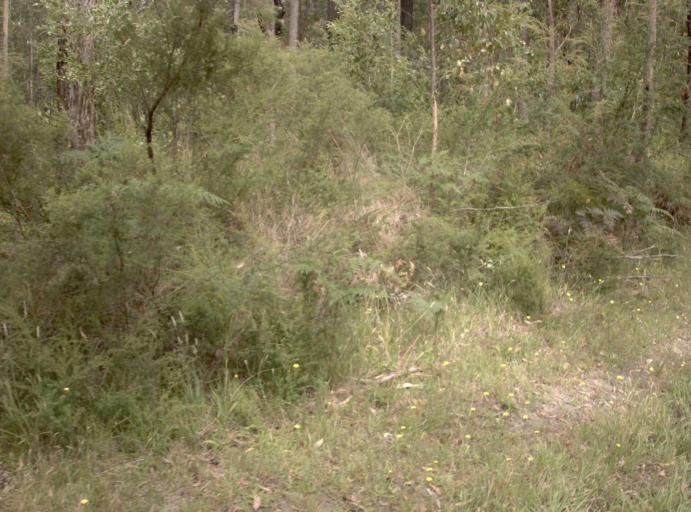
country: AU
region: Victoria
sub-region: Latrobe
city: Morwell
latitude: -38.0596
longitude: 146.4245
